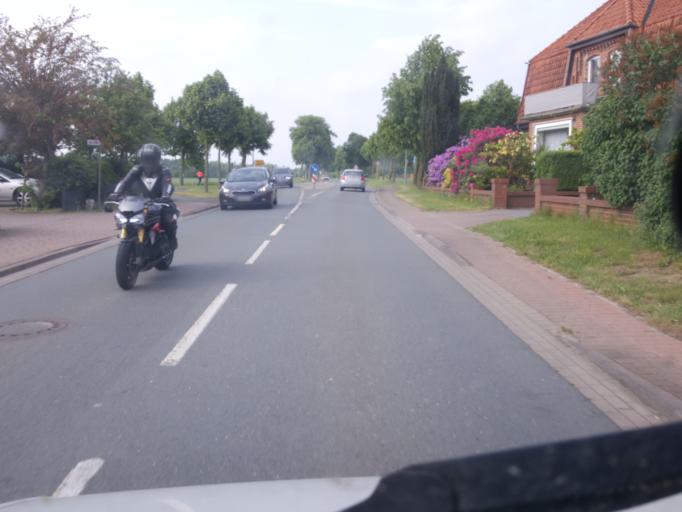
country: DE
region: Lower Saxony
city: Marklohe
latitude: 52.6472
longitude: 9.1471
